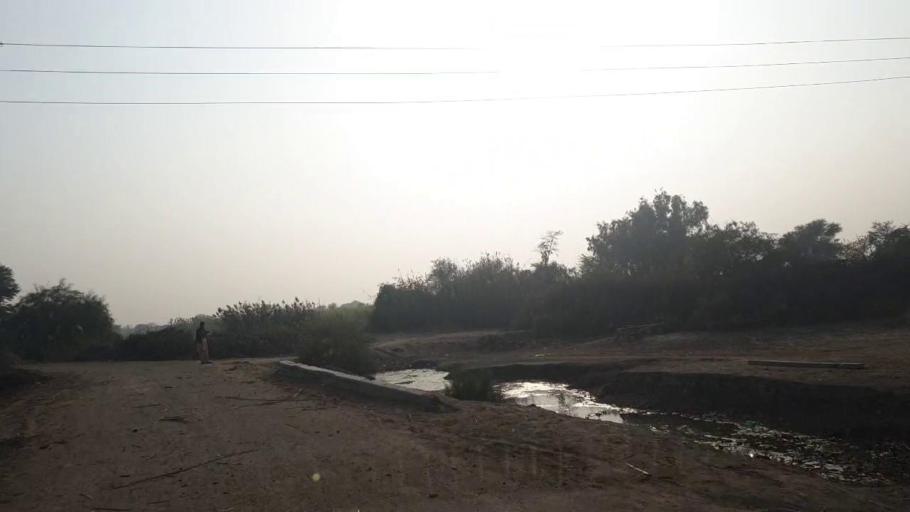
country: PK
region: Sindh
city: Shahdadpur
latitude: 25.8587
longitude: 68.5958
